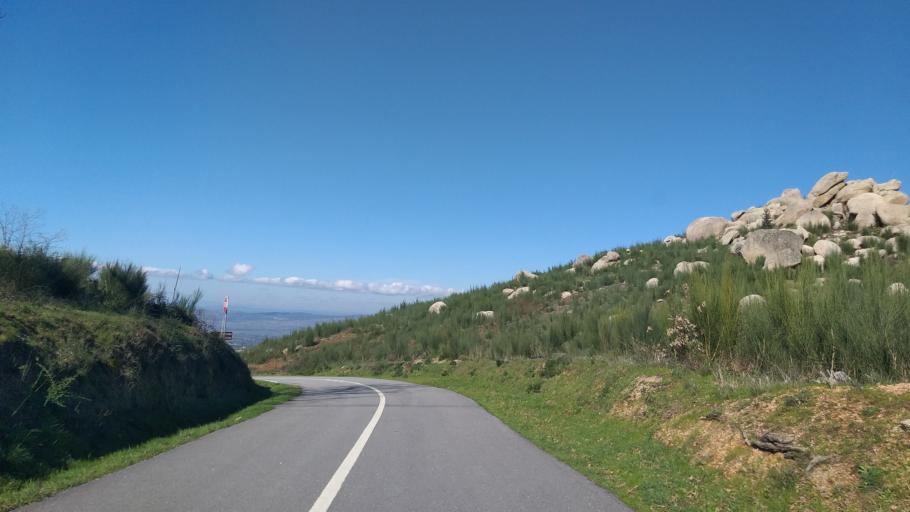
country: PT
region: Guarda
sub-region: Manteigas
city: Manteigas
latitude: 40.4668
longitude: -7.6150
